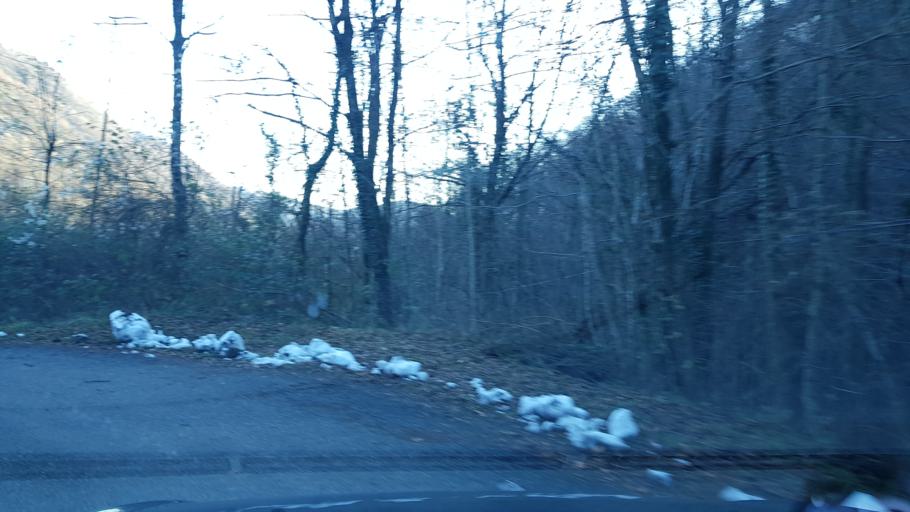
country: IT
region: Friuli Venezia Giulia
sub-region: Provincia di Udine
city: Savogna
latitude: 46.1798
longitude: 13.5369
